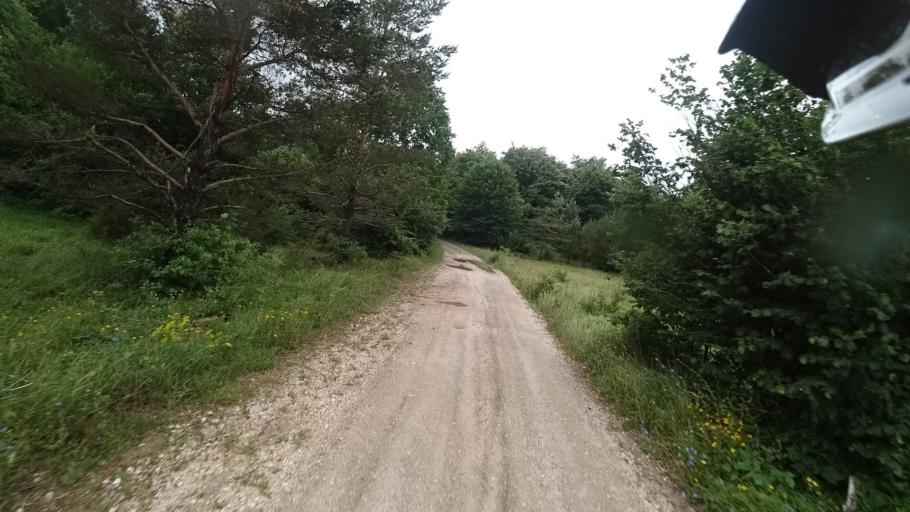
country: HR
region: Karlovacka
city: Plaski
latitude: 44.9050
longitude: 15.4139
